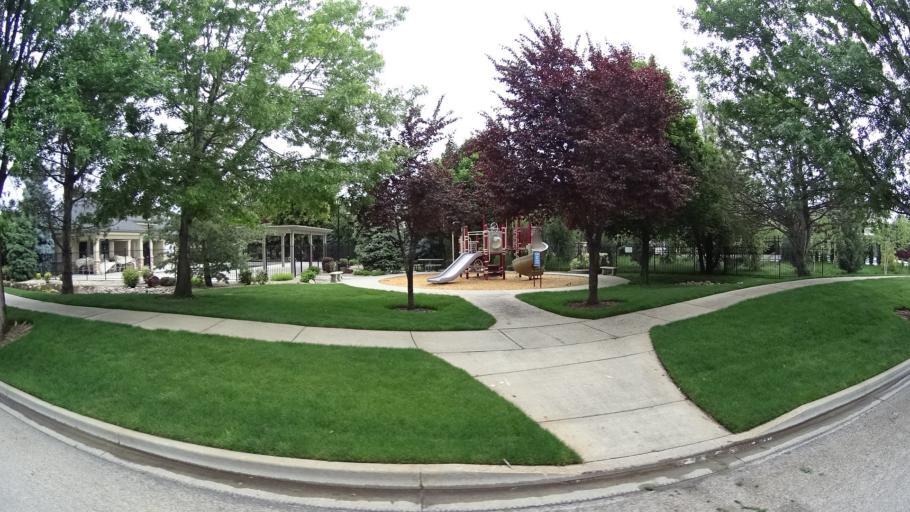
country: US
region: Idaho
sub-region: Ada County
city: Eagle
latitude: 43.6780
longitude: -116.3375
